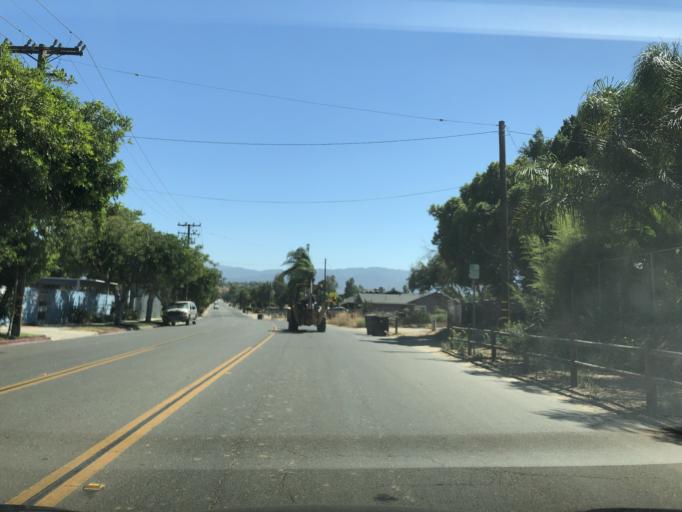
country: US
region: California
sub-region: Riverside County
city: Norco
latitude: 33.9149
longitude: -117.5482
